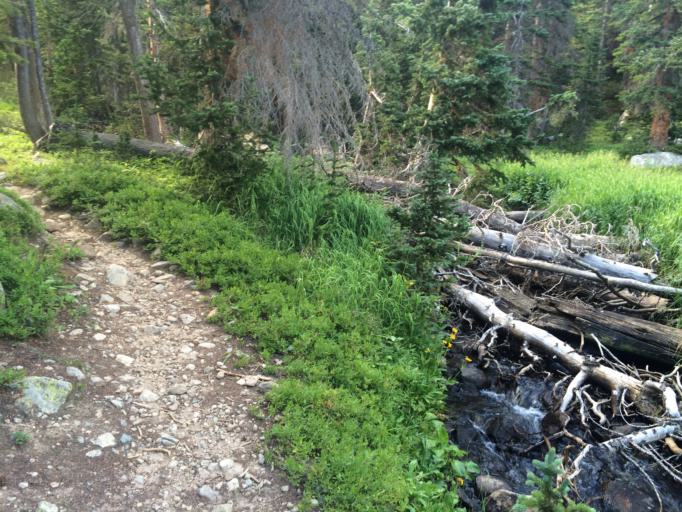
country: US
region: Colorado
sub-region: Larimer County
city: Estes Park
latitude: 40.1773
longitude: -105.6188
